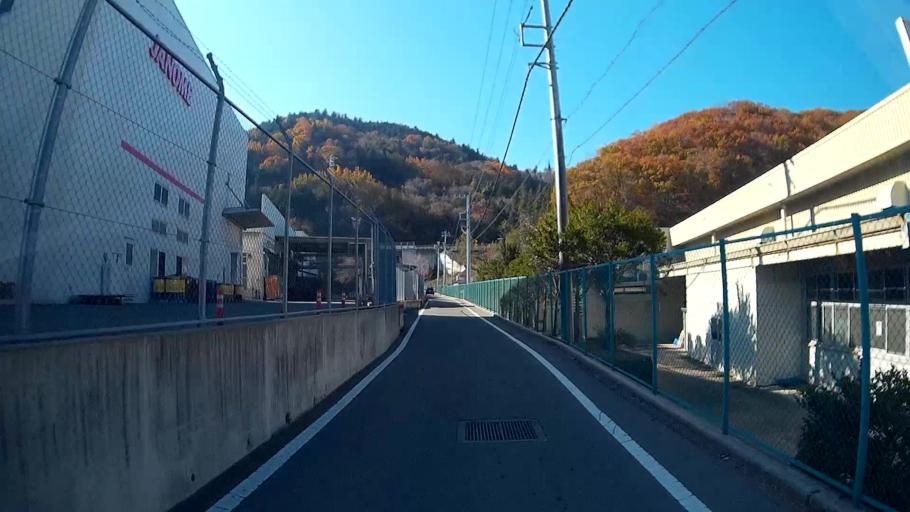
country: JP
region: Yamanashi
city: Otsuki
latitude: 35.5638
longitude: 138.9354
